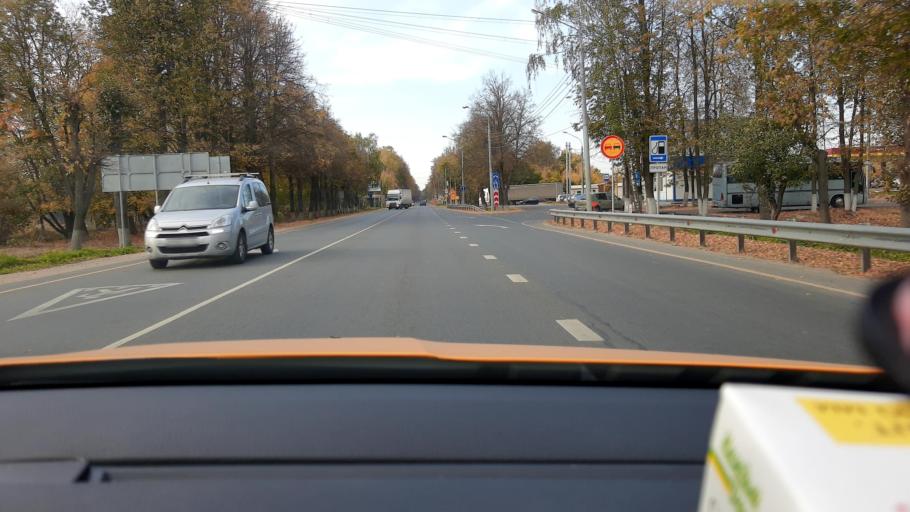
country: RU
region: Moskovskaya
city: Arkhangel'skoye
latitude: 55.7990
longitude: 37.3055
